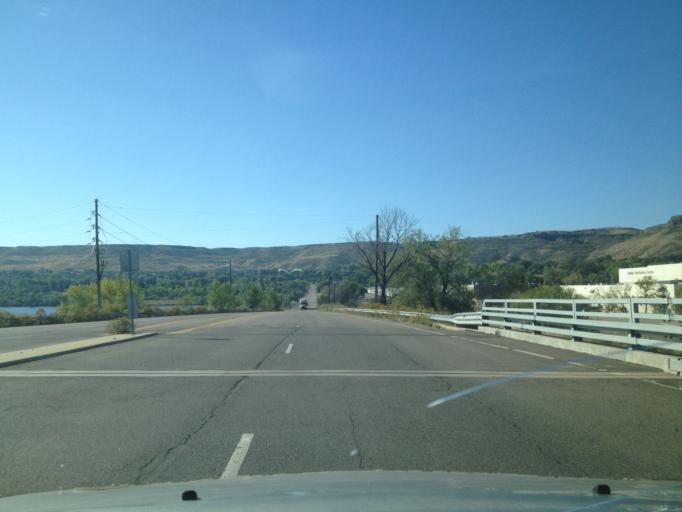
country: US
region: Colorado
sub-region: Jefferson County
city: Applewood
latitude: 39.7714
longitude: -105.1749
